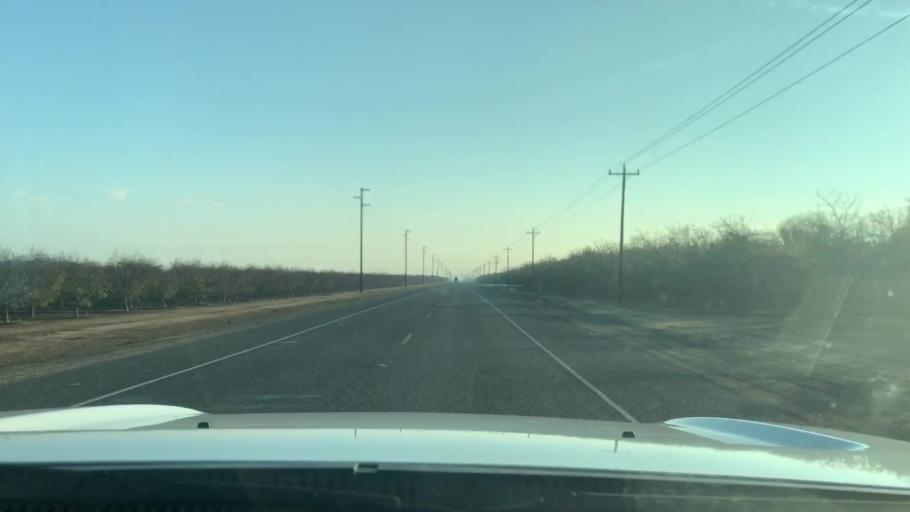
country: US
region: California
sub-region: Kern County
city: Wasco
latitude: 35.6012
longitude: -119.4643
